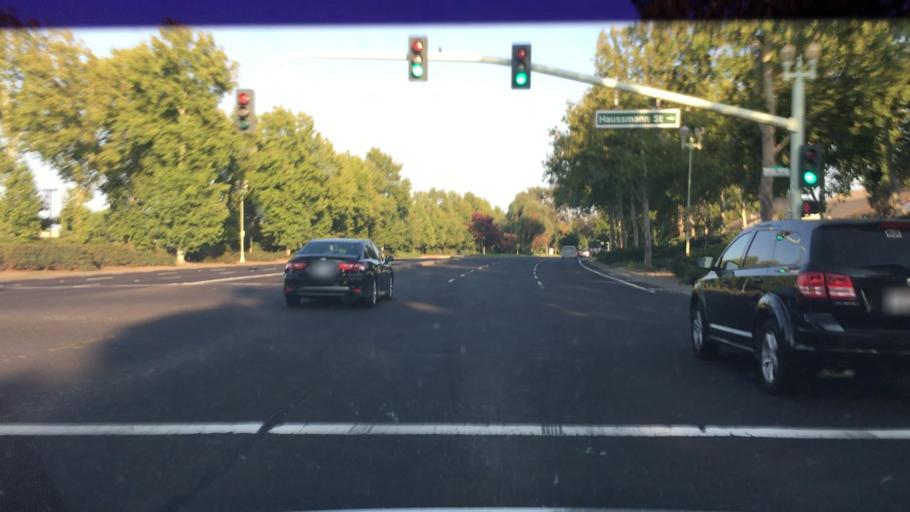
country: US
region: California
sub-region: Sacramento County
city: Laguna
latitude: 38.4272
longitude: -121.4658
